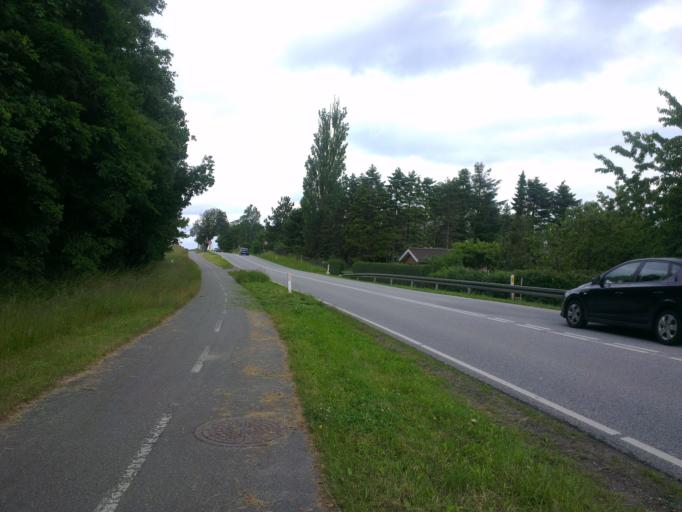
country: DK
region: Capital Region
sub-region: Frederikssund Kommune
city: Skibby
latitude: 55.6758
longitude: 11.9391
